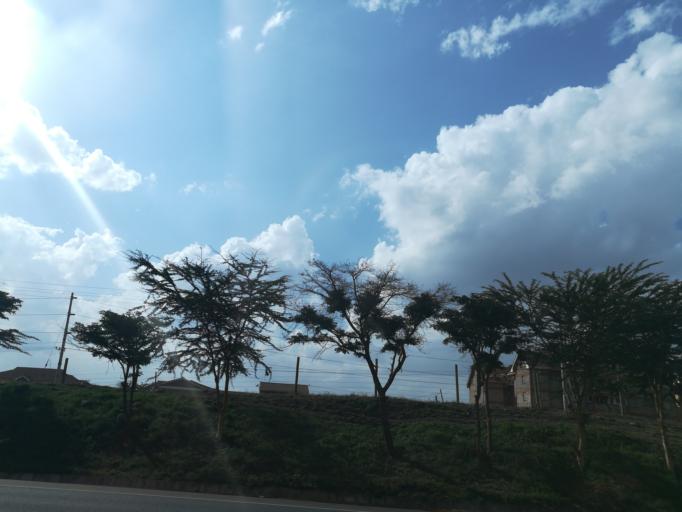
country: KE
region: Nairobi Area
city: Pumwani
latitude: -1.3292
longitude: 36.8357
